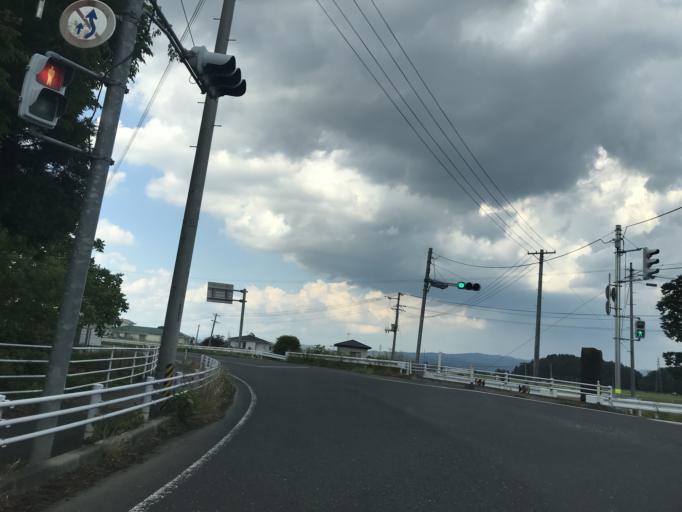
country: JP
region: Miyagi
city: Wakuya
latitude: 38.6478
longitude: 141.2168
